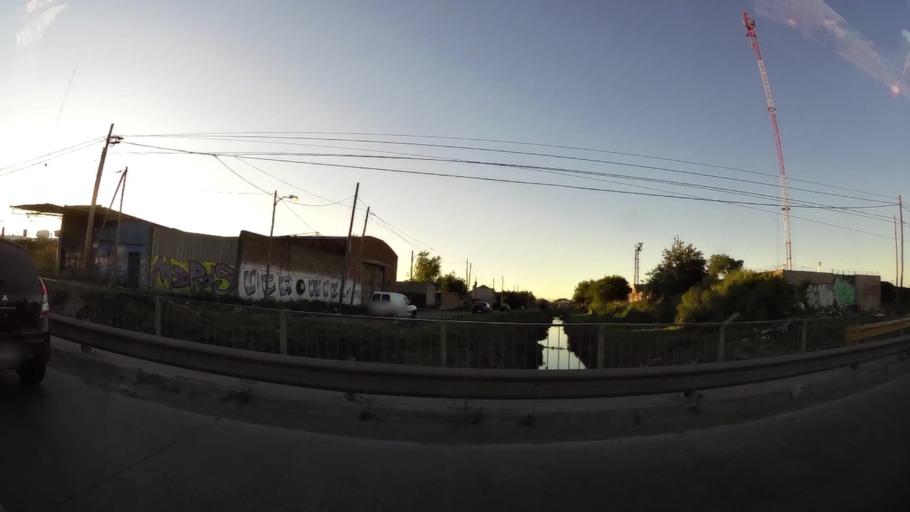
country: AR
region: Buenos Aires
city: Pontevedra
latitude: -34.7466
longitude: -58.6103
